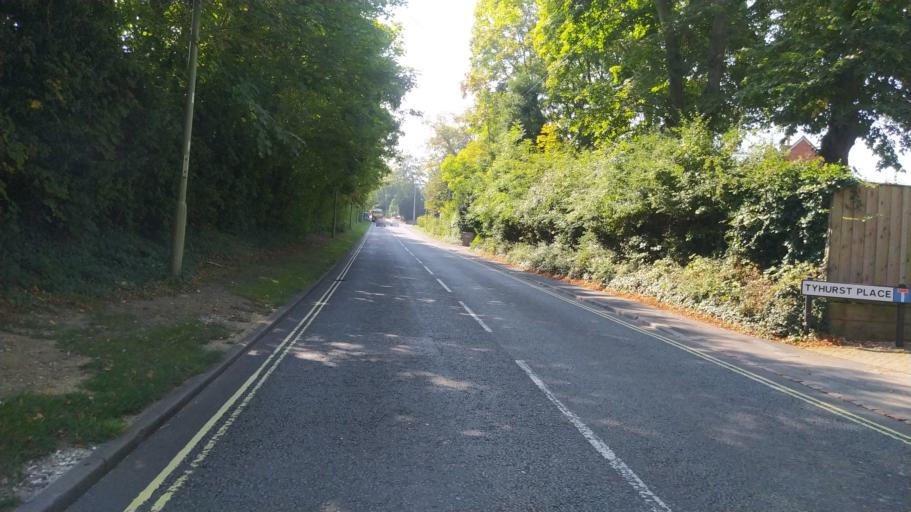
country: GB
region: England
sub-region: Hampshire
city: Andover
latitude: 51.1995
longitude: -1.4806
